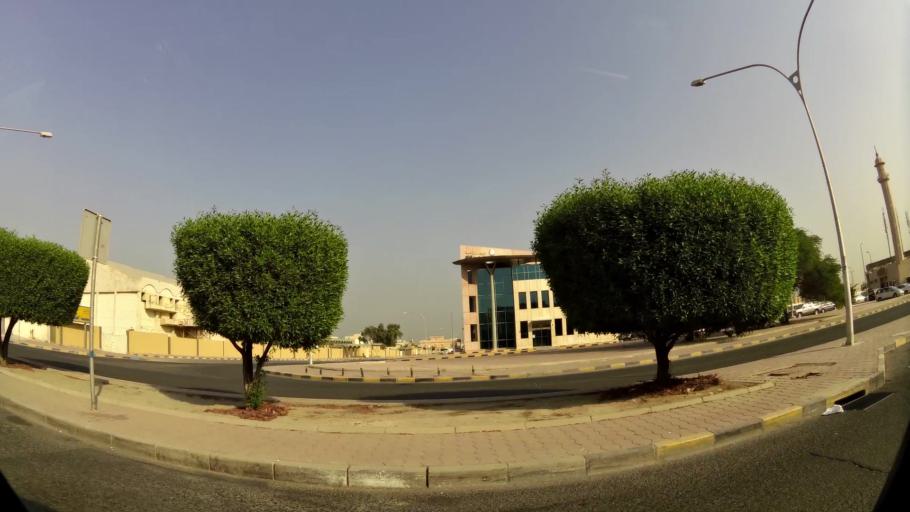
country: KW
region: Al Ahmadi
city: Al Manqaf
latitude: 29.1039
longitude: 48.1052
